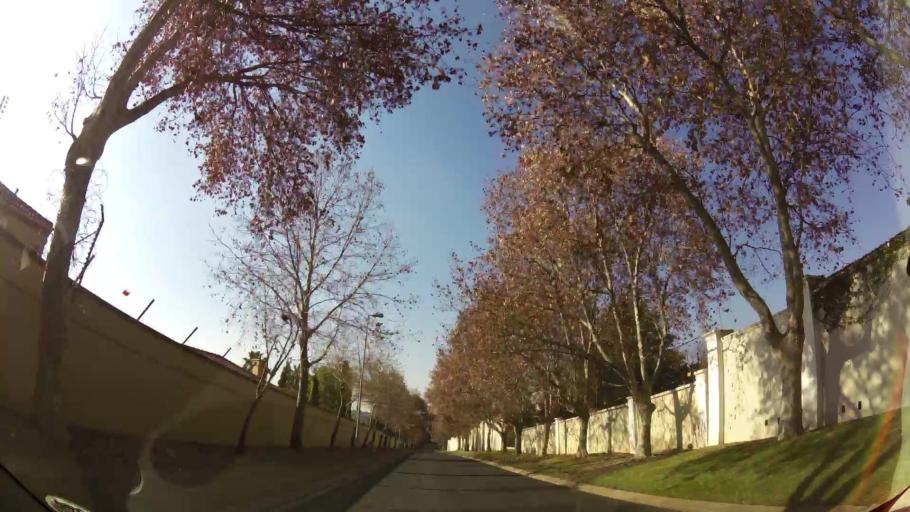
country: ZA
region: Gauteng
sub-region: City of Johannesburg Metropolitan Municipality
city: Diepsloot
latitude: -26.0643
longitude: 28.0039
